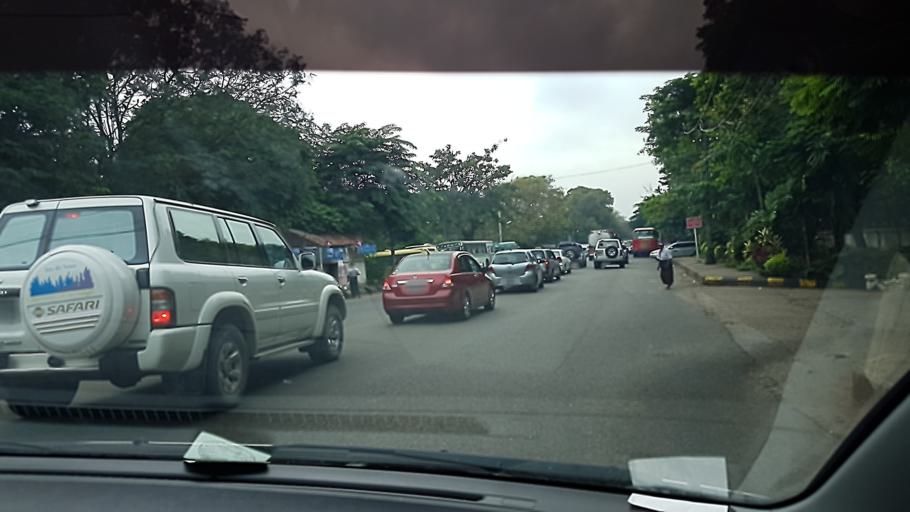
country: MM
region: Yangon
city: Yangon
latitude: 16.8172
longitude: 96.1260
